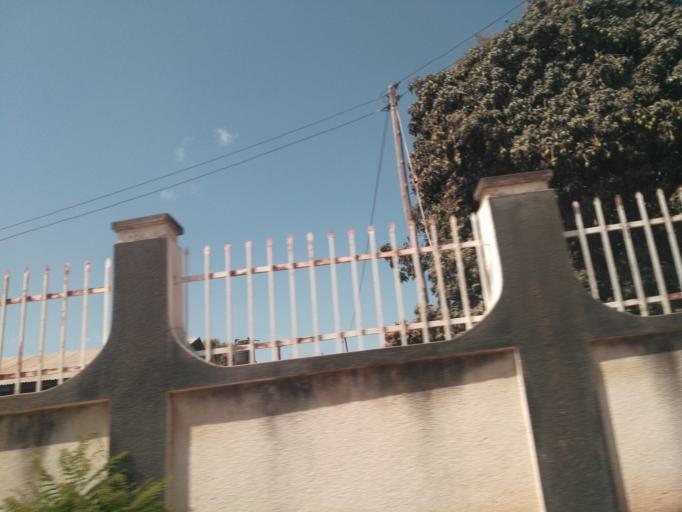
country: TZ
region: Dodoma
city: Dodoma
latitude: -6.1617
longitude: 35.7581
